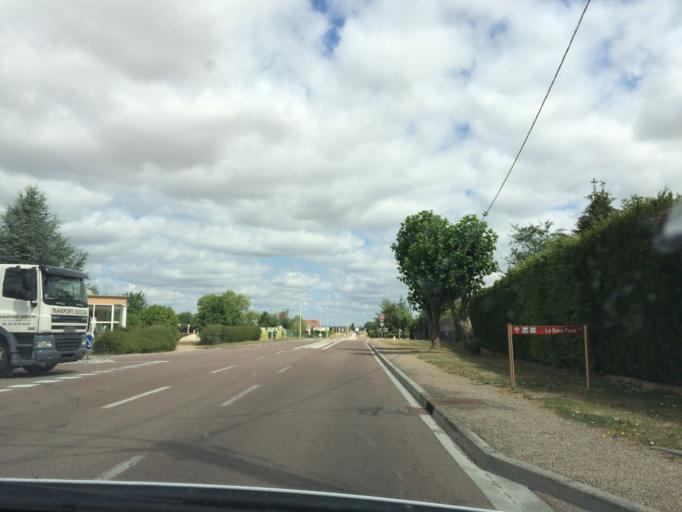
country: FR
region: Bourgogne
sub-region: Departement de la Cote-d'Or
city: Fenay
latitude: 47.2327
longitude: 5.0617
